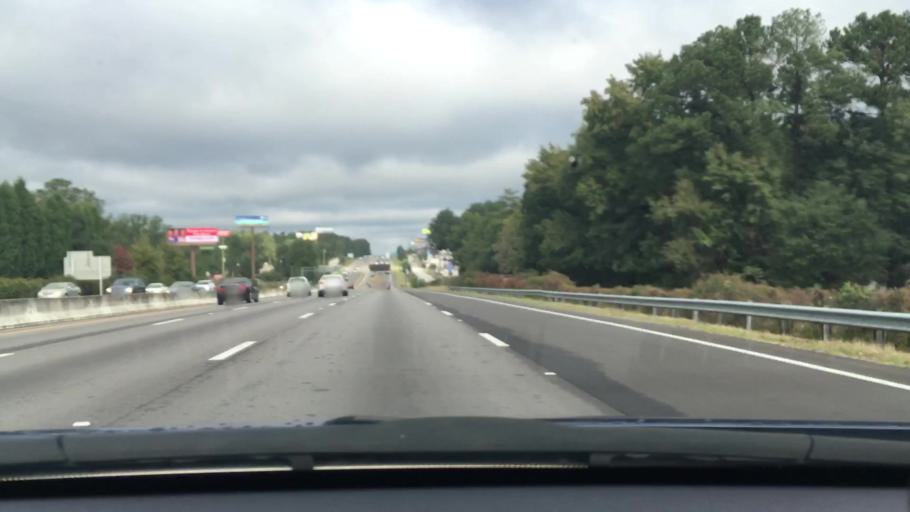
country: US
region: South Carolina
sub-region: Lexington County
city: Saint Andrews
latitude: 34.0482
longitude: -81.1214
